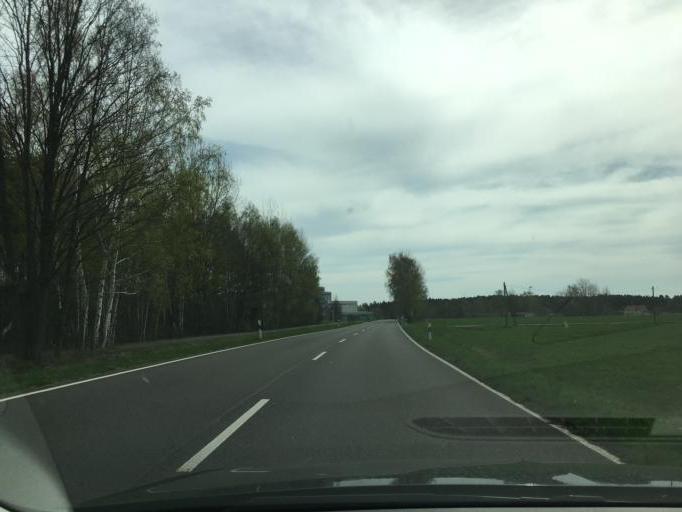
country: DE
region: Brandenburg
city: Tschernitz
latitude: 51.5787
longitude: 14.5977
